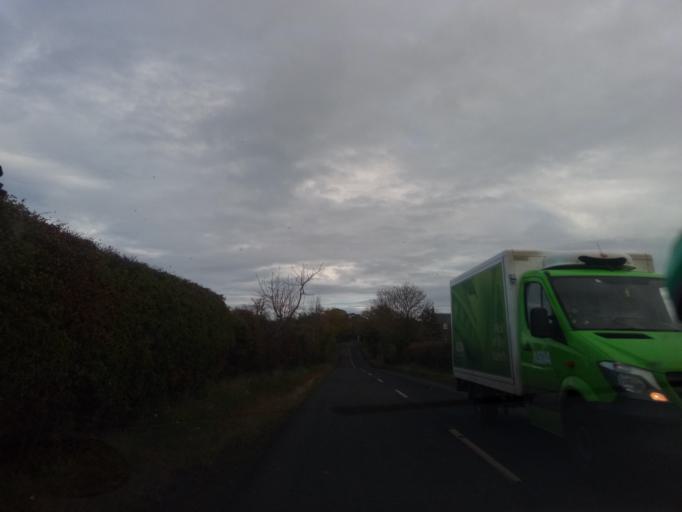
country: GB
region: Scotland
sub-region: The Scottish Borders
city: Eyemouth
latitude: 55.8518
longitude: -2.1073
